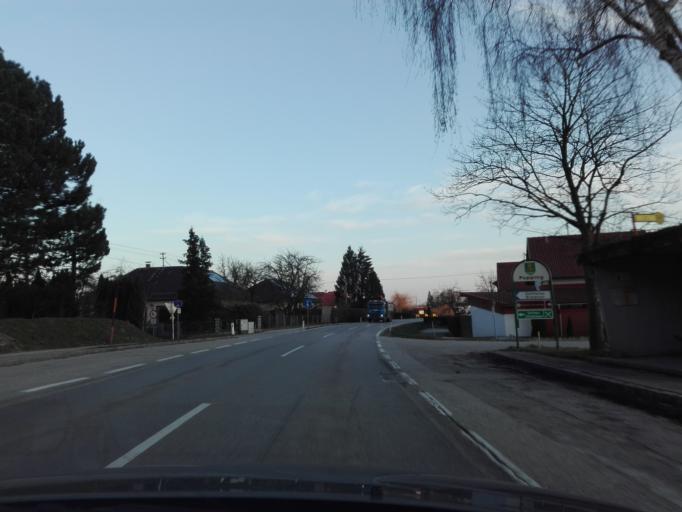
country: AT
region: Upper Austria
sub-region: Politischer Bezirk Urfahr-Umgebung
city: Feldkirchen an der Donau
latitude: 48.3293
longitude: 14.0089
